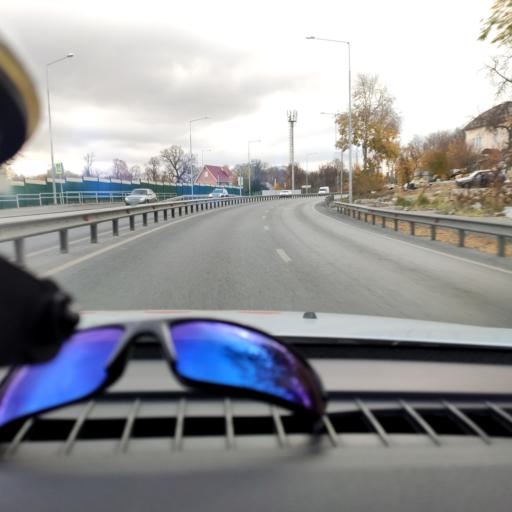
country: RU
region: Samara
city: Volzhskiy
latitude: 53.3650
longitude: 50.1999
